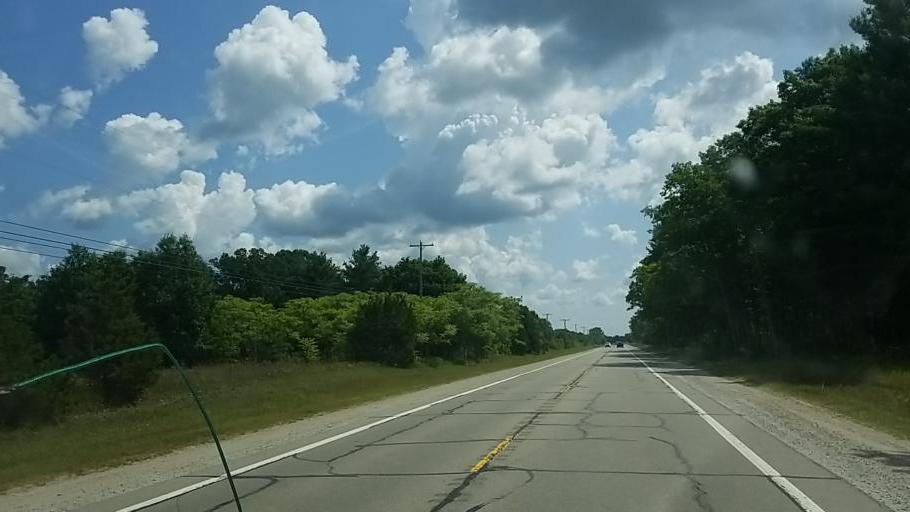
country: US
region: Michigan
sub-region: Muskegon County
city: Wolf Lake
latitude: 43.2353
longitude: -86.0392
